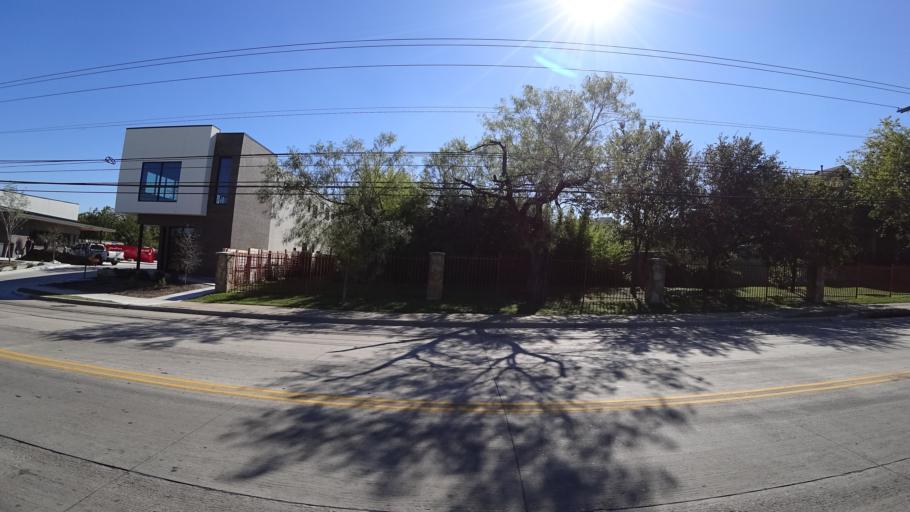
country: US
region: Texas
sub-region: Travis County
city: Austin
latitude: 30.2237
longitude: -97.7043
